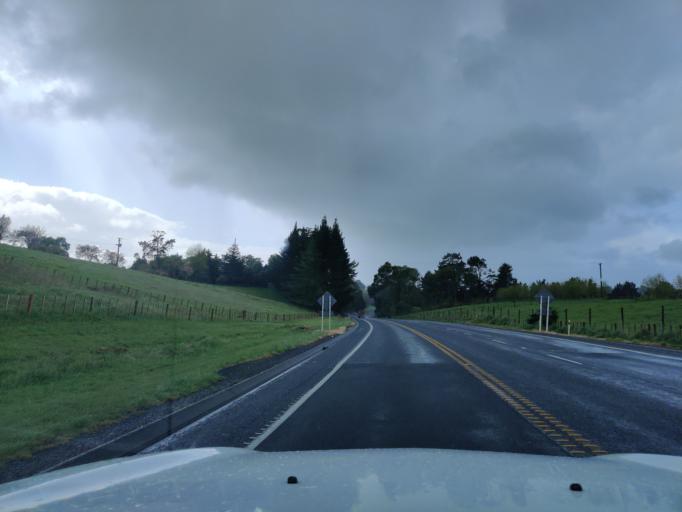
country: NZ
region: Waikato
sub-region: Waipa District
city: Cambridge
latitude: -37.9399
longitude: 175.5784
